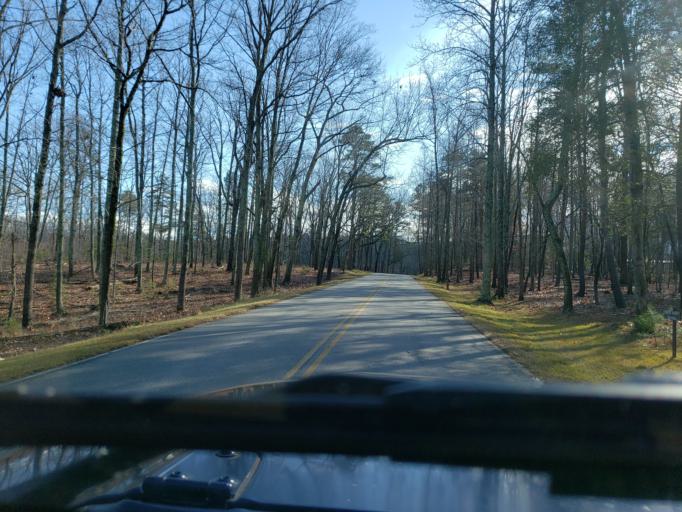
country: US
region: North Carolina
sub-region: Cleveland County
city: White Plains
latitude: 35.1440
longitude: -81.3874
